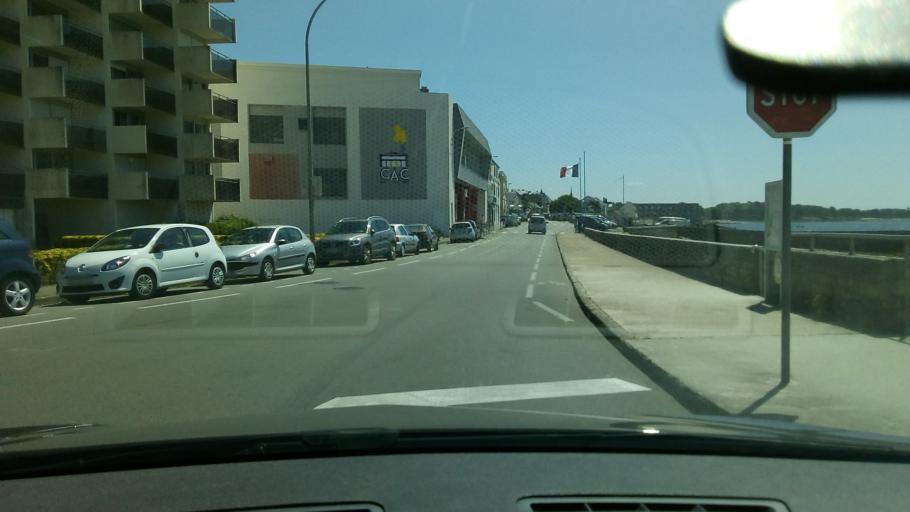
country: FR
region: Brittany
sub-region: Departement du Finistere
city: Concarneau
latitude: 47.8703
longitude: -3.9228
